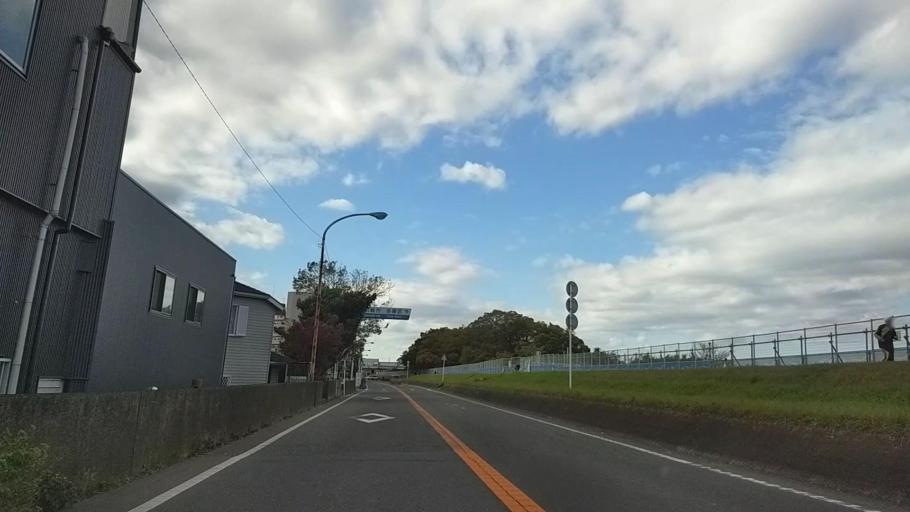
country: JP
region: Tokyo
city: Chofugaoka
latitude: 35.6156
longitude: 139.5991
